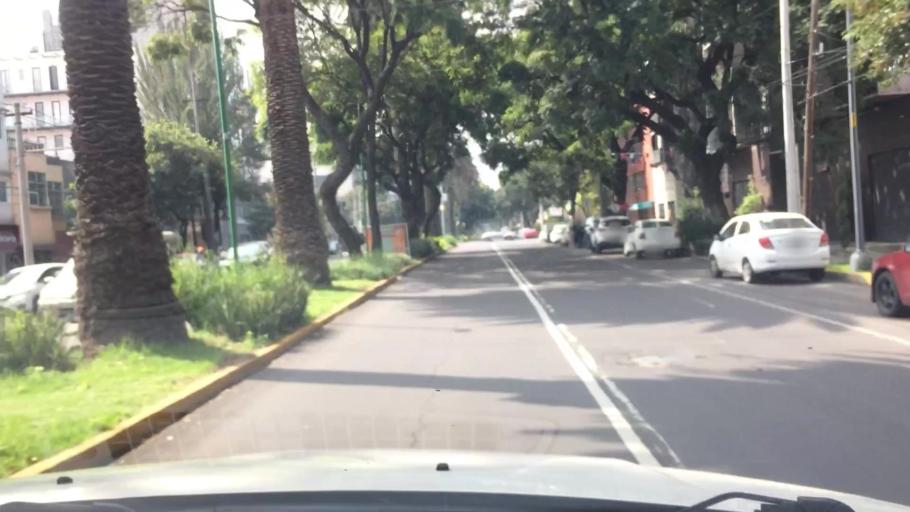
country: MX
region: Mexico City
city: Colonia del Valle
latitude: 19.3795
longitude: -99.1533
